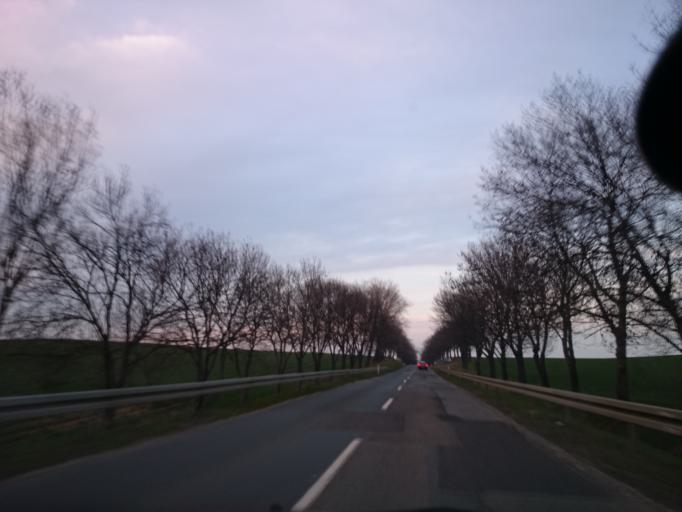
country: PL
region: Opole Voivodeship
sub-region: Powiat prudnicki
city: Biala
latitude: 50.3637
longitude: 17.6479
